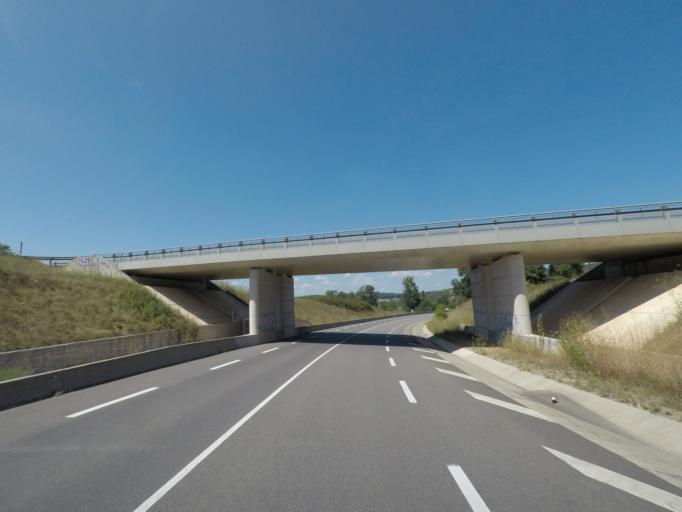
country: FR
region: Midi-Pyrenees
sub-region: Departement du Lot
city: Figeac
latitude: 44.5884
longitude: 1.9980
